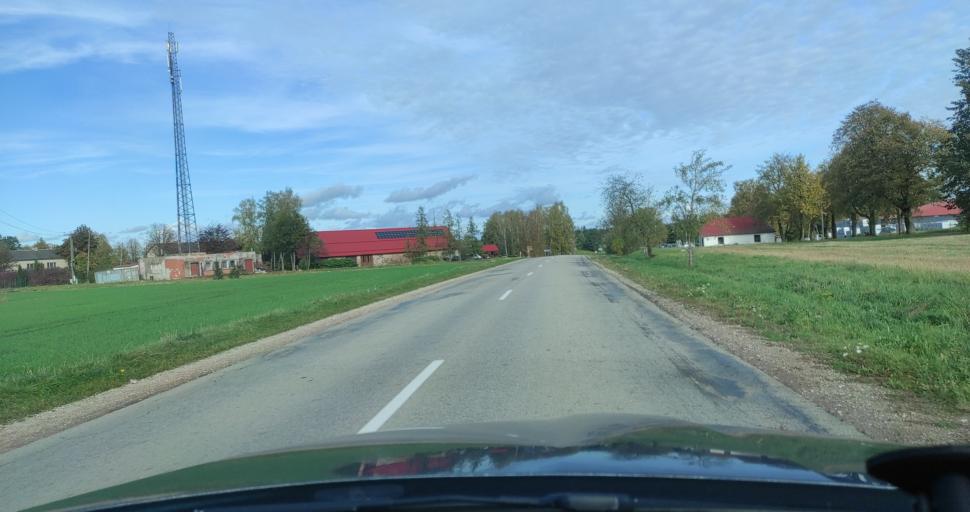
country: LV
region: Jaunpils
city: Jaunpils
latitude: 56.7280
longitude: 23.0096
